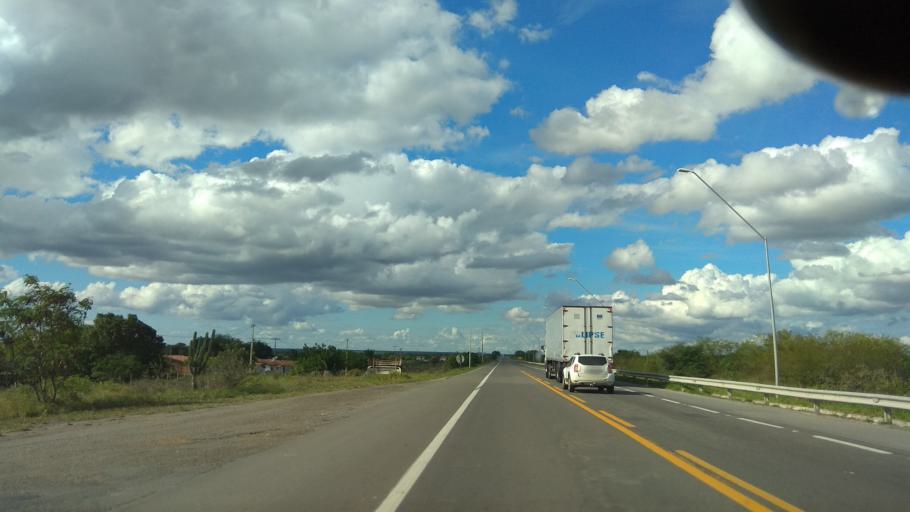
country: BR
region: Bahia
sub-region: Castro Alves
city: Castro Alves
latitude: -12.6130
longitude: -39.5691
